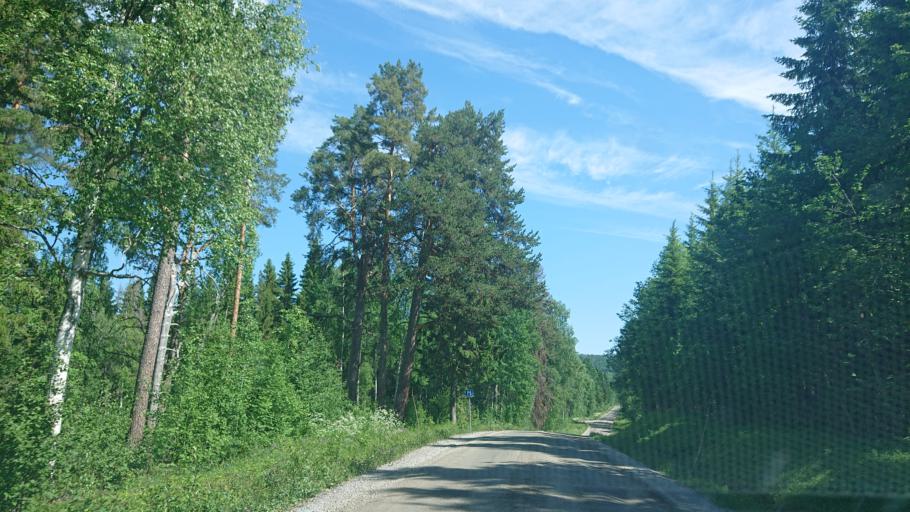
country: SE
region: Vaesternorrland
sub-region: Solleftea Kommun
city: Solleftea
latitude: 62.9707
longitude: 17.1646
